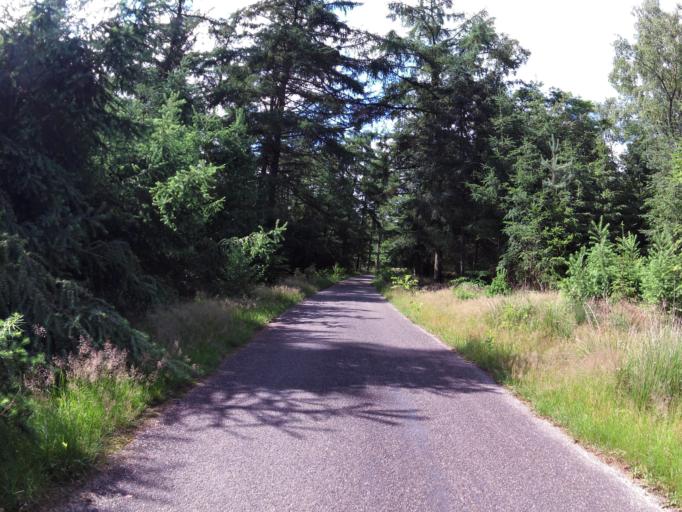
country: NL
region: North Brabant
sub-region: Gemeente Valkenswaard
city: Valkenswaard
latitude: 51.3297
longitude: 5.5076
